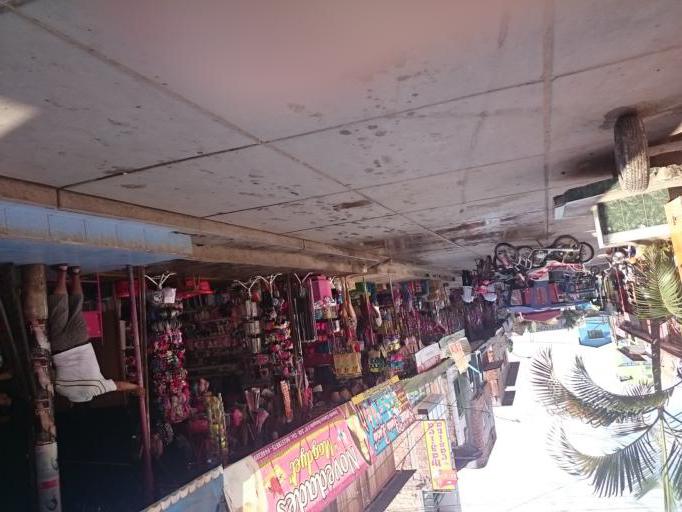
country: PE
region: Ucayali
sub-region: Provincia de Coronel Portillo
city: Pucallpa
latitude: -8.3855
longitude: -74.5347
